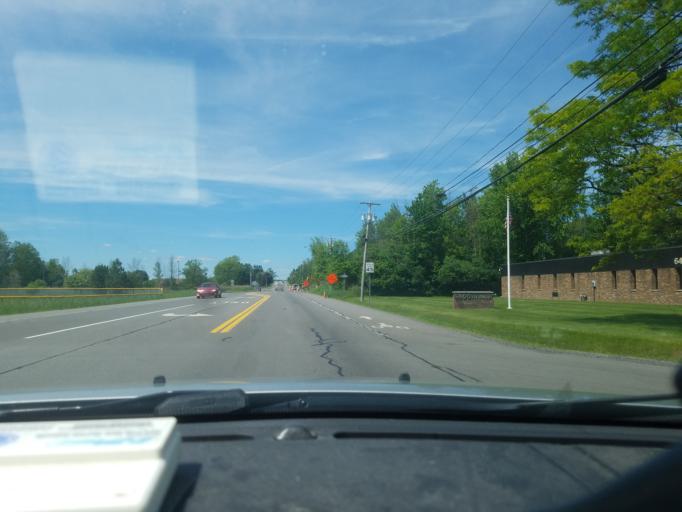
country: US
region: New York
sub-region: Onondaga County
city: East Syracuse
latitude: 43.0805
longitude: -76.0584
